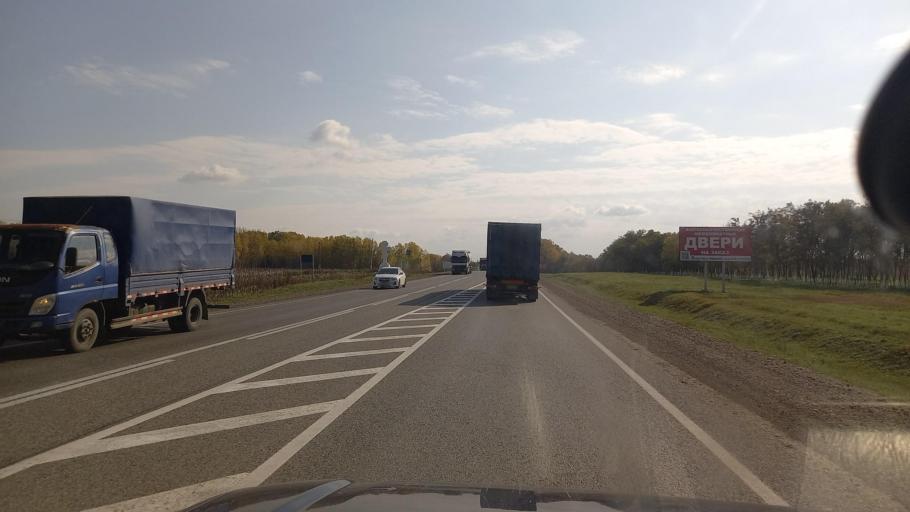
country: RU
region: Krasnodarskiy
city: Novoukrainskiy
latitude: 44.8878
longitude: 38.0794
